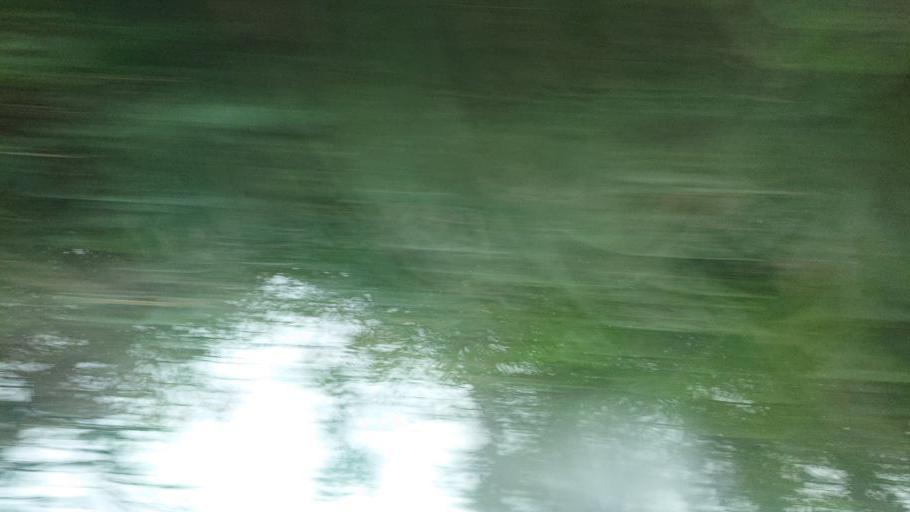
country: TW
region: Taiwan
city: Lugu
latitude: 23.5963
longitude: 120.7143
